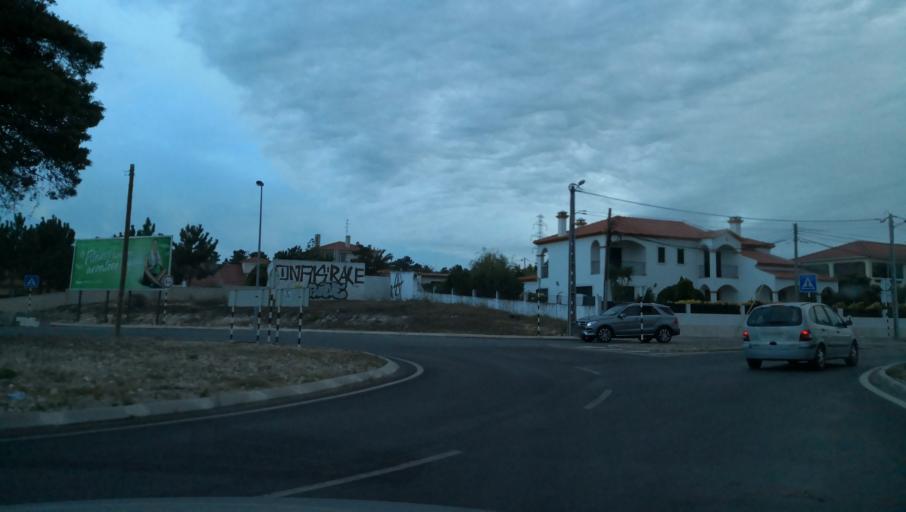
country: PT
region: Setubal
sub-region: Seixal
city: Amora
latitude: 38.5952
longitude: -9.1455
